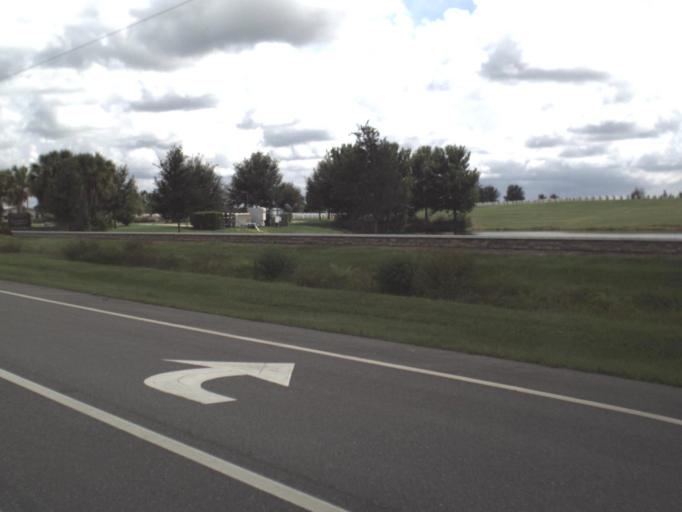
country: US
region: Florida
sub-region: Sarasota County
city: Lake Sarasota
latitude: 27.2472
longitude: -82.3800
